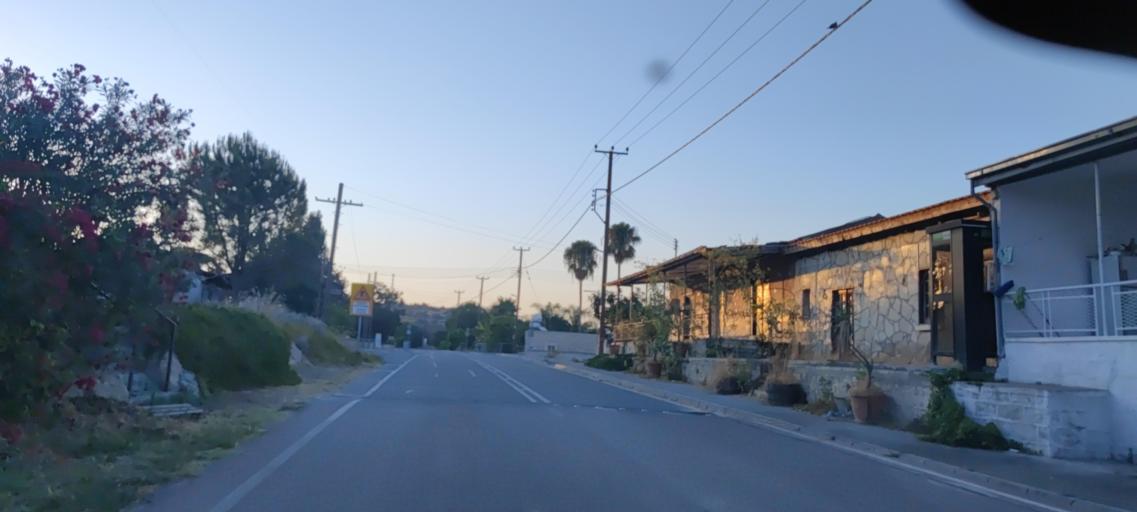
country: CY
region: Limassol
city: Sotira
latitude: 34.6765
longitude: 32.7917
